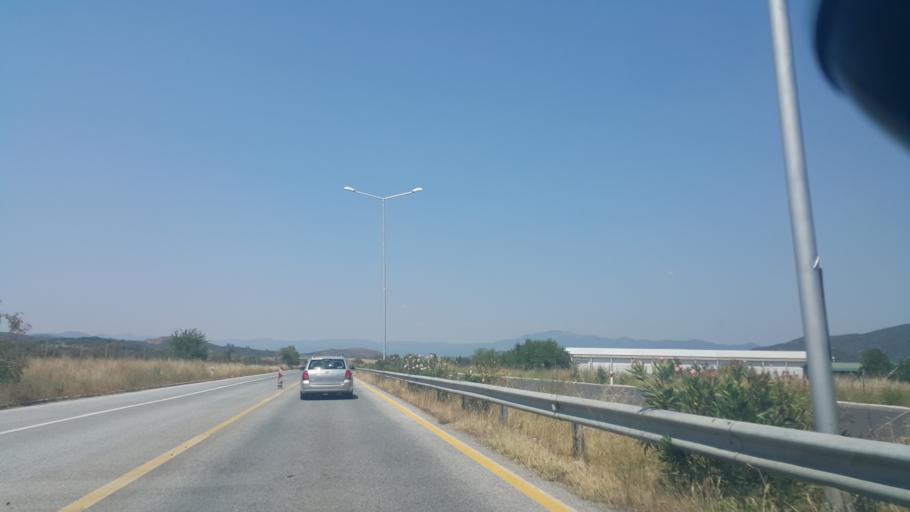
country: MK
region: Gevgelija
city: Gevgelija
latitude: 41.2071
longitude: 22.4951
